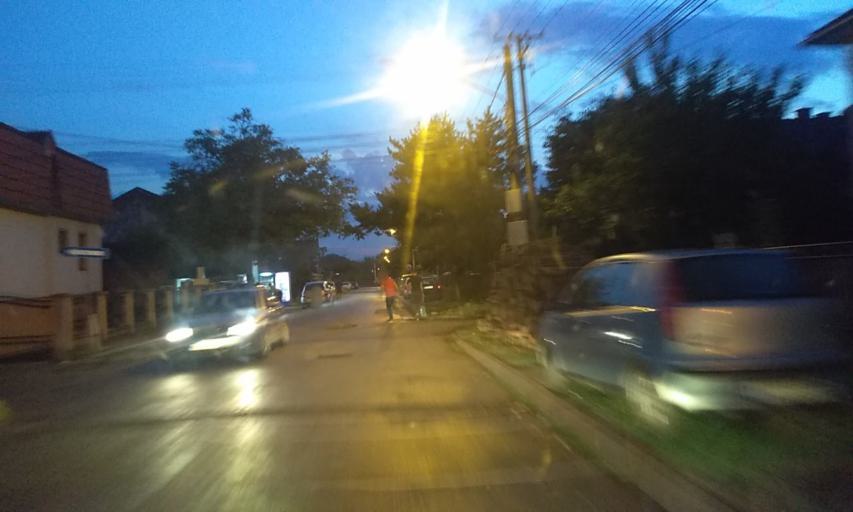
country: RS
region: Central Serbia
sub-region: Nisavski Okrug
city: Nis
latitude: 43.3314
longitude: 21.9159
